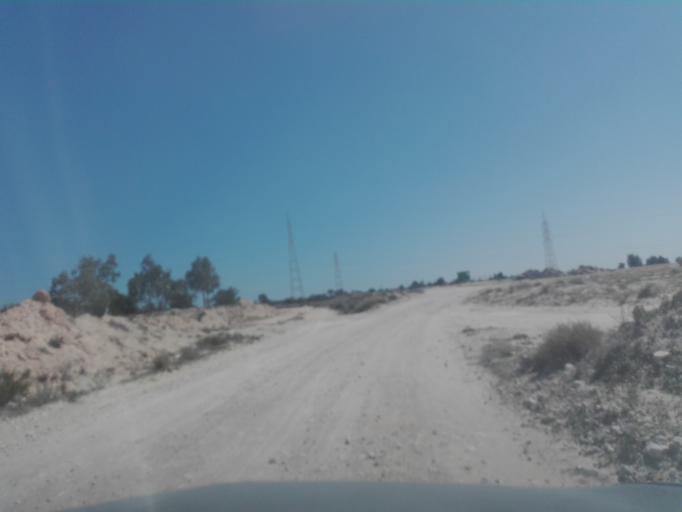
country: TN
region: Qabis
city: Gabes
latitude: 33.8746
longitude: 10.0284
